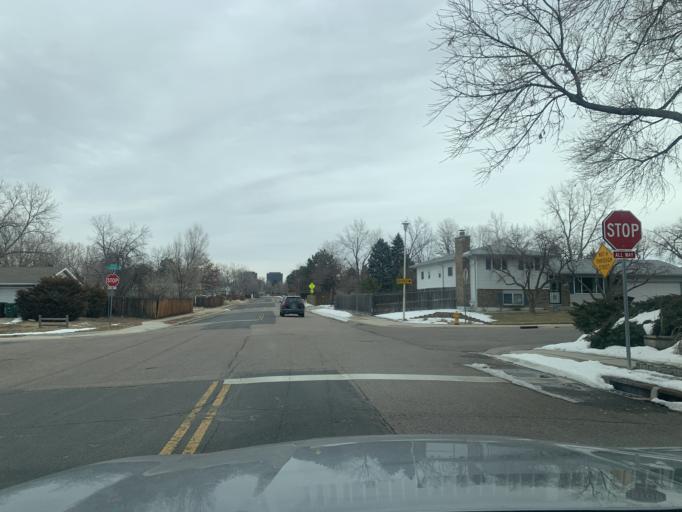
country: US
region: Colorado
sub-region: Arapahoe County
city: Glendale
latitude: 39.6613
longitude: -104.8788
